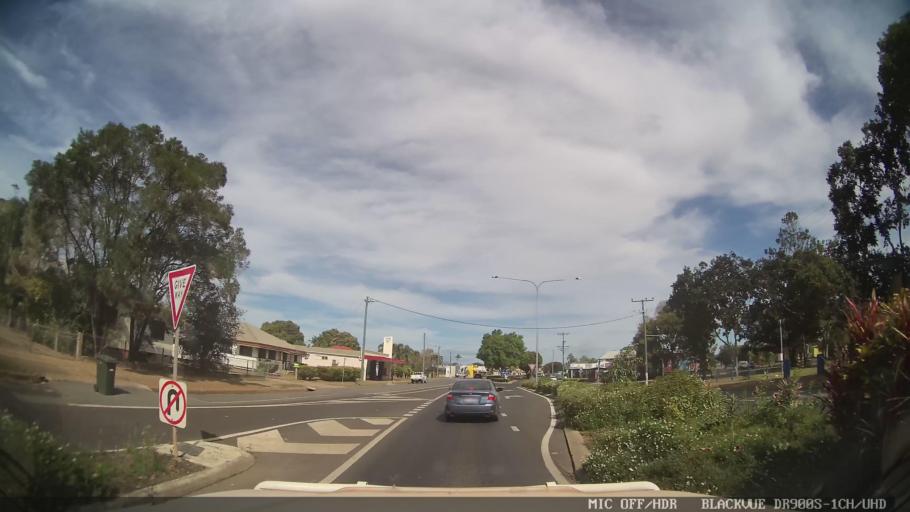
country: AU
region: Queensland
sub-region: Tablelands
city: Mareeba
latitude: -16.9874
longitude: 145.4205
